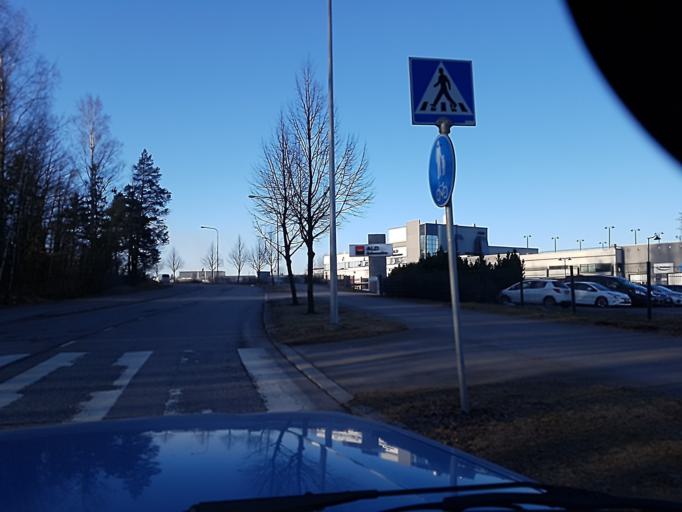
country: FI
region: Uusimaa
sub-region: Helsinki
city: Vantaa
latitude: 60.2959
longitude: 24.9901
